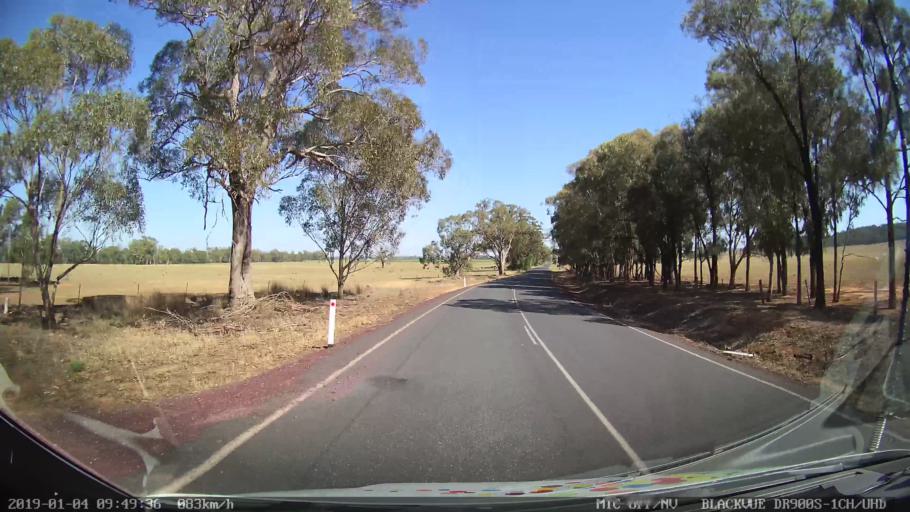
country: AU
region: New South Wales
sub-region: Cabonne
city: Canowindra
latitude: -33.5937
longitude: 148.4176
